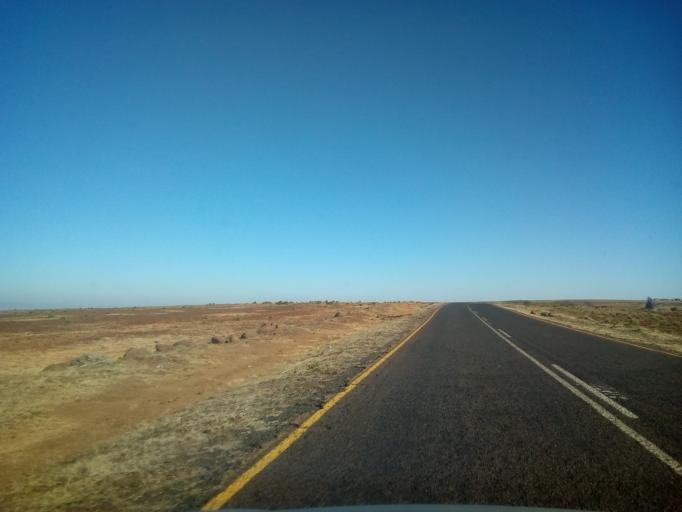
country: LS
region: Berea
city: Teyateyaneng
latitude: -29.2572
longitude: 27.7524
